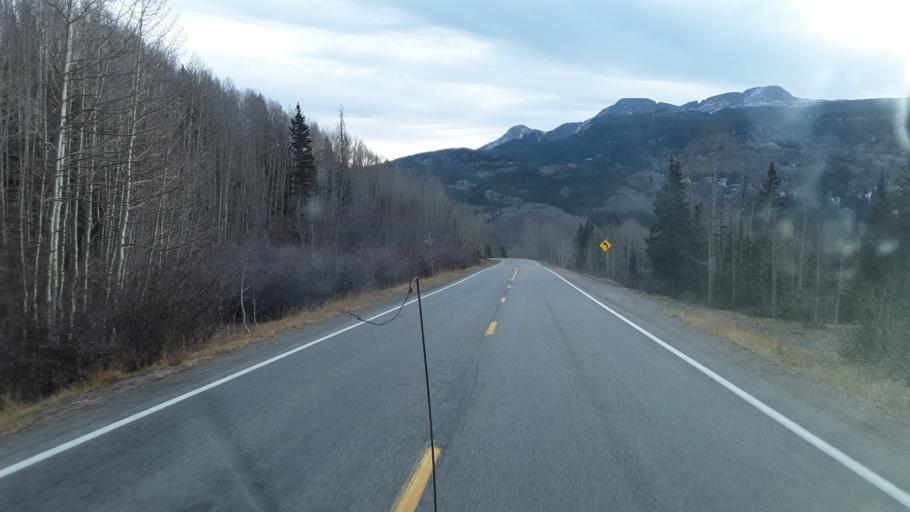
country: US
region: Colorado
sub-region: San Juan County
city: Silverton
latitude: 37.7118
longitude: -107.7611
